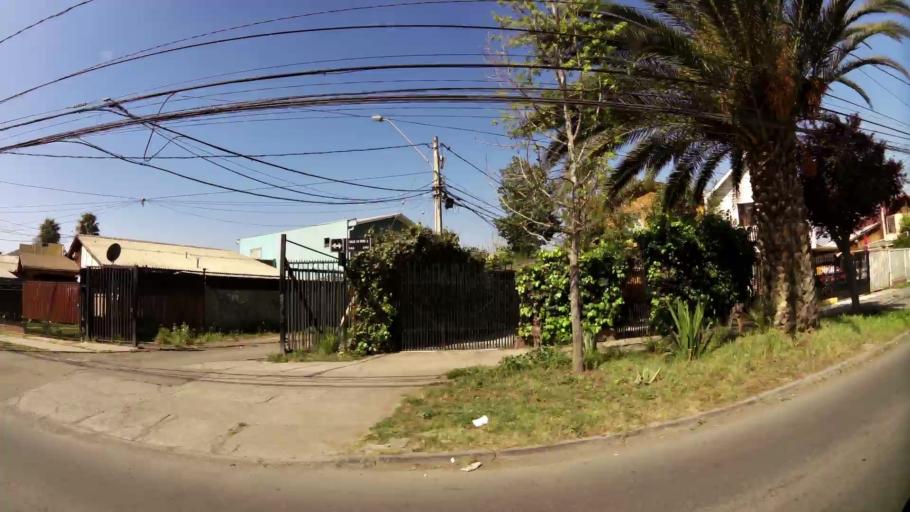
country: CL
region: Santiago Metropolitan
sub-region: Provincia de Santiago
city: Lo Prado
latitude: -33.3529
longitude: -70.7340
